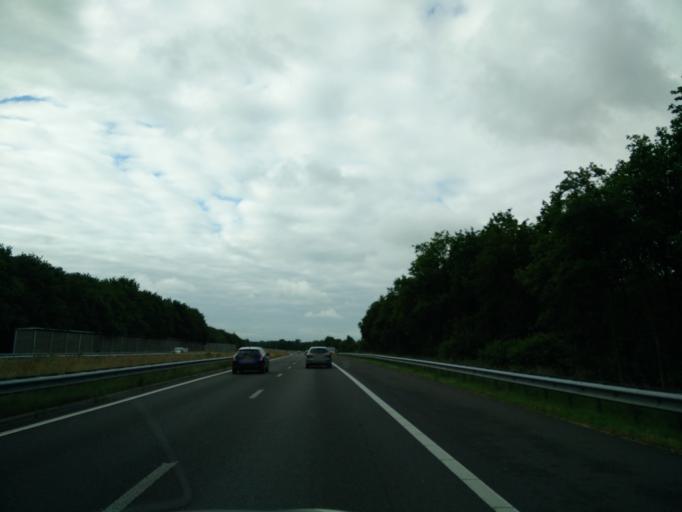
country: NL
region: Drenthe
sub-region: Gemeente Hoogeveen
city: Hoogeveen
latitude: 52.7745
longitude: 6.4472
